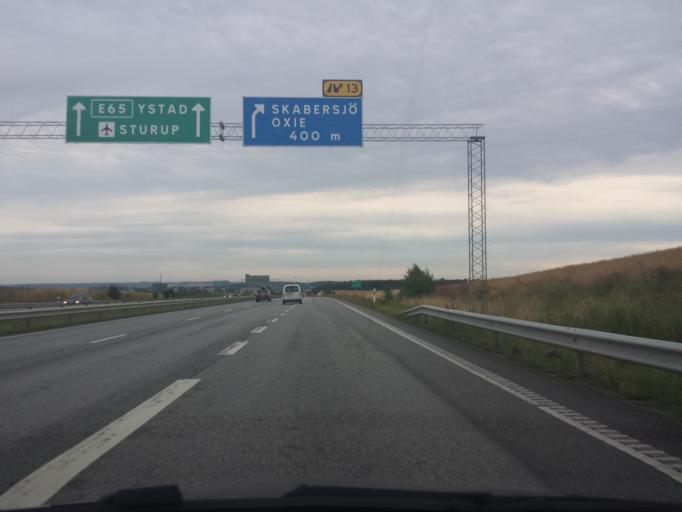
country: SE
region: Skane
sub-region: Malmo
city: Oxie
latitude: 55.5577
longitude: 13.0886
